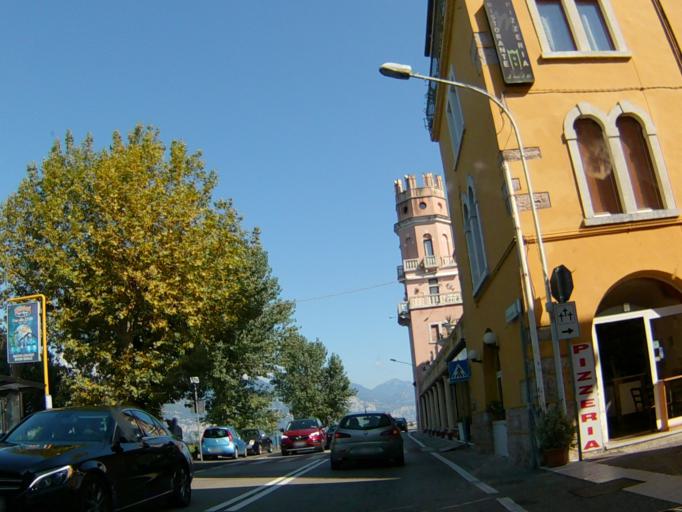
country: IT
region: Veneto
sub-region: Provincia di Verona
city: San Zeno di Montagna
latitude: 45.6549
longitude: 10.7229
